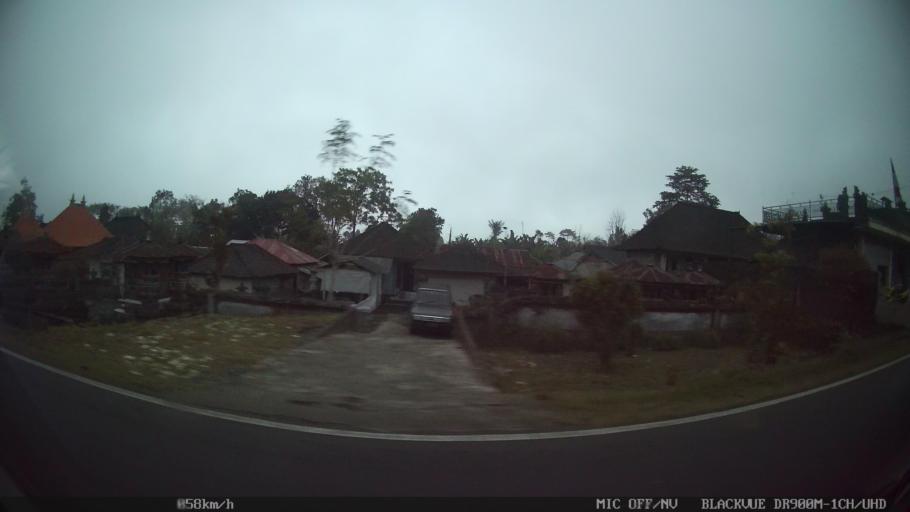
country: ID
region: Bali
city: Banjar Kedisan
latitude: -8.3063
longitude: 115.3062
